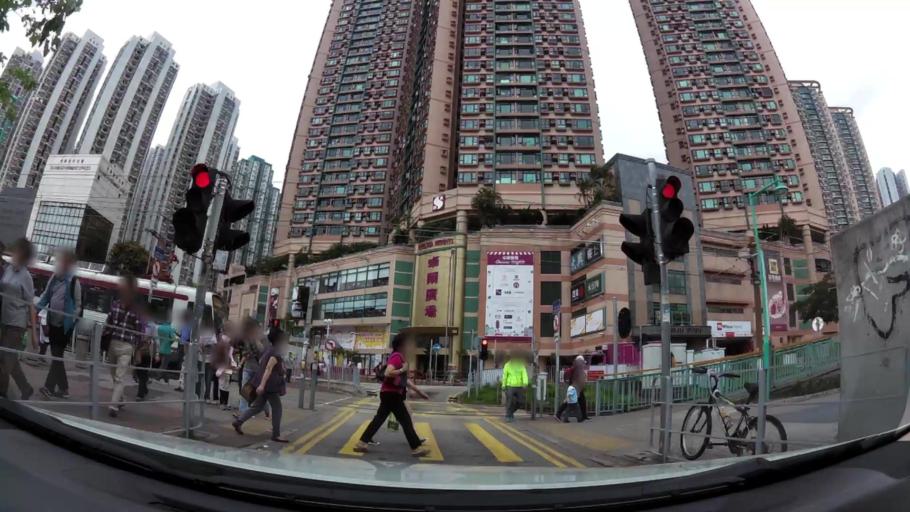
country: HK
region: Tuen Mun
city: Tuen Mun
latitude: 22.4001
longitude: 113.9745
